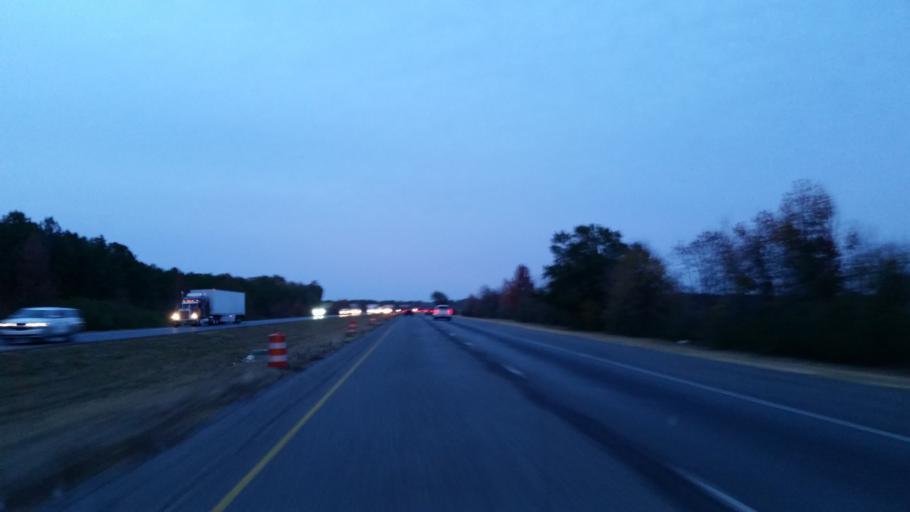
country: US
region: Alabama
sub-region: Tuscaloosa County
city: Tuscaloosa
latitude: 33.1409
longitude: -87.6266
